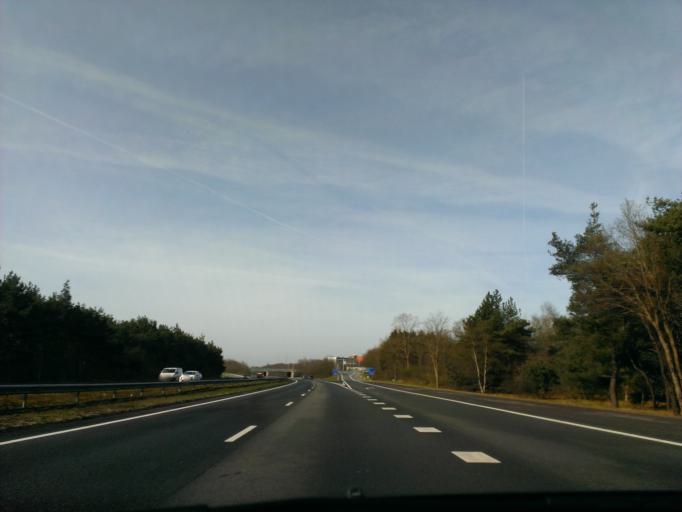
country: NL
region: Gelderland
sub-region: Gemeente Harderwijk
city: Harderwijk
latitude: 52.3399
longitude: 5.6508
